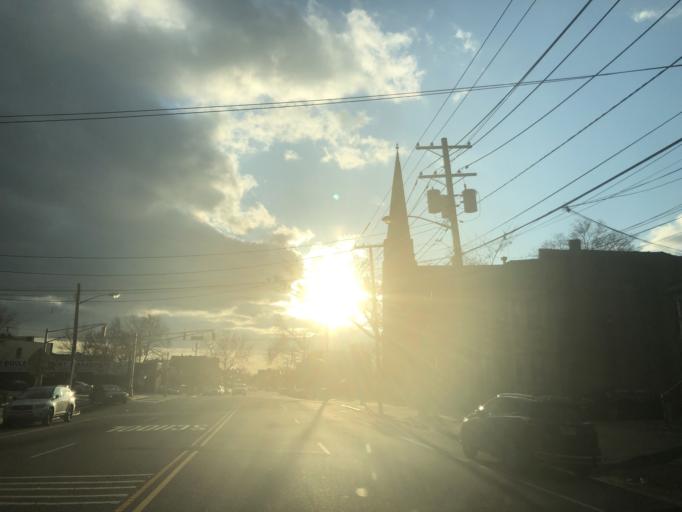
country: US
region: New Jersey
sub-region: Hudson County
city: Jersey City
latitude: 40.7023
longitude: -74.0919
